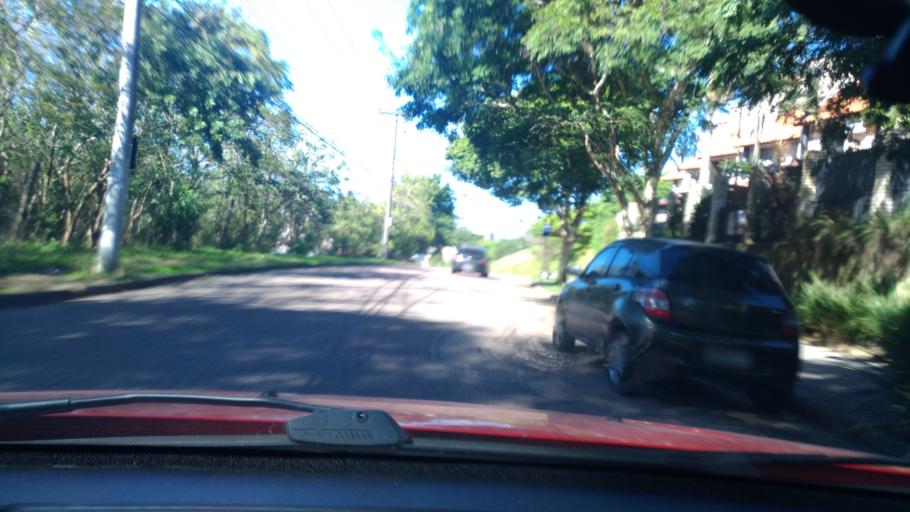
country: BR
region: Rio Grande do Sul
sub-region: Porto Alegre
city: Porto Alegre
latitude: -30.0350
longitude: -51.1457
